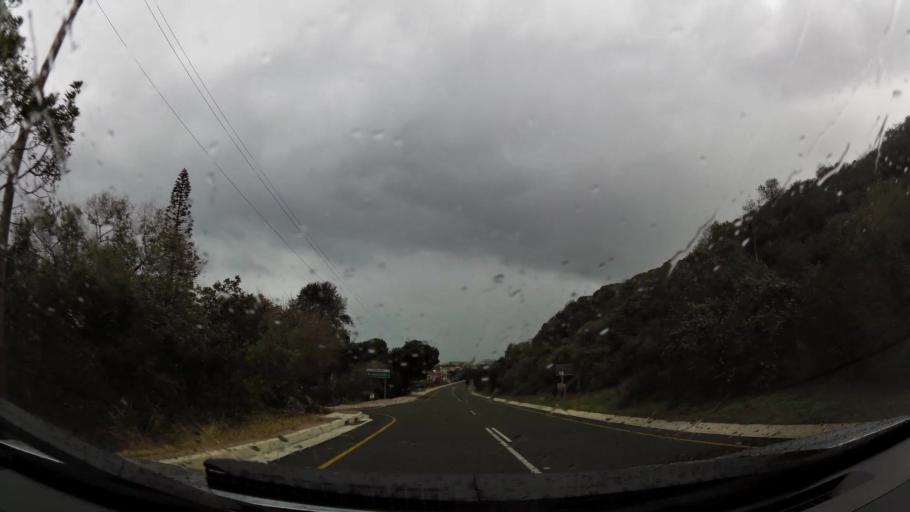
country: ZA
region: Western Cape
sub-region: Eden District Municipality
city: George
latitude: -34.0491
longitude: 22.3005
